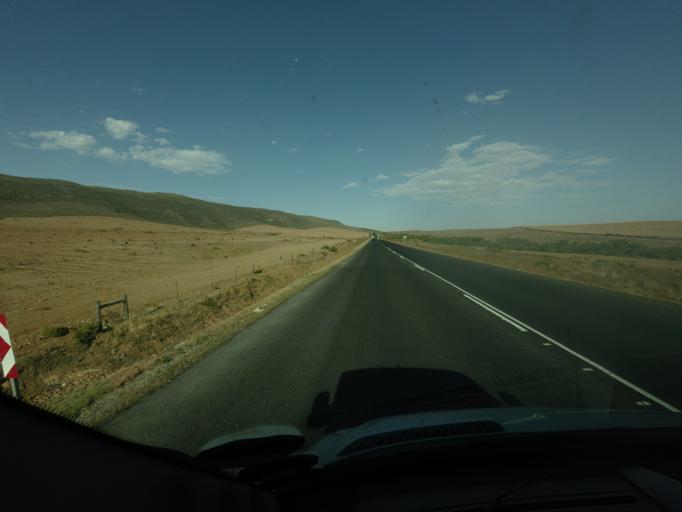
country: ZA
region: Western Cape
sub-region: Cape Winelands District Municipality
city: Ashton
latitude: -34.0980
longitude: 20.1624
